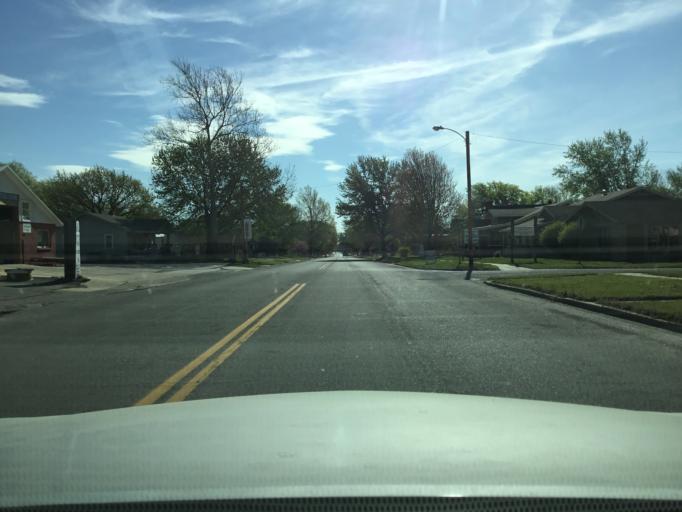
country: US
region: Kansas
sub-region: Neosho County
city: Chanute
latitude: 37.6819
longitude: -95.4653
